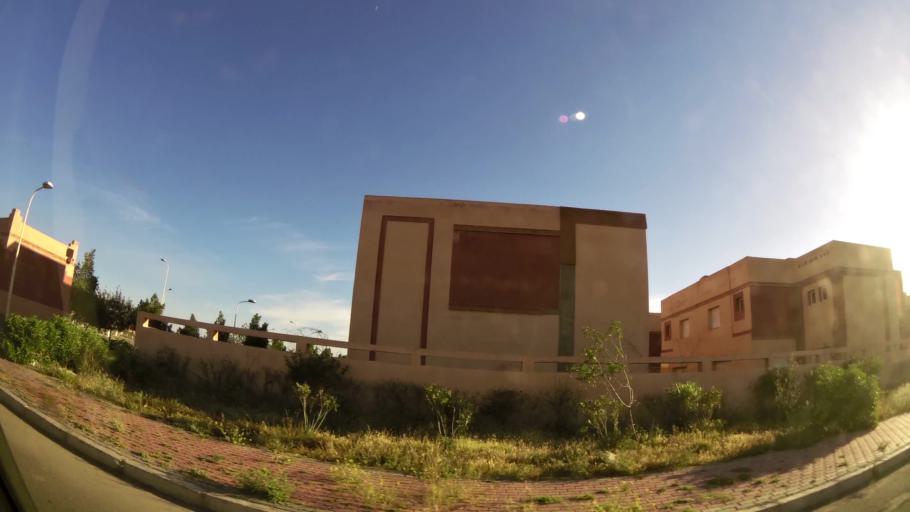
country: MA
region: Marrakech-Tensift-Al Haouz
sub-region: Marrakech
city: Marrakesh
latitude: 31.7618
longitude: -8.1080
